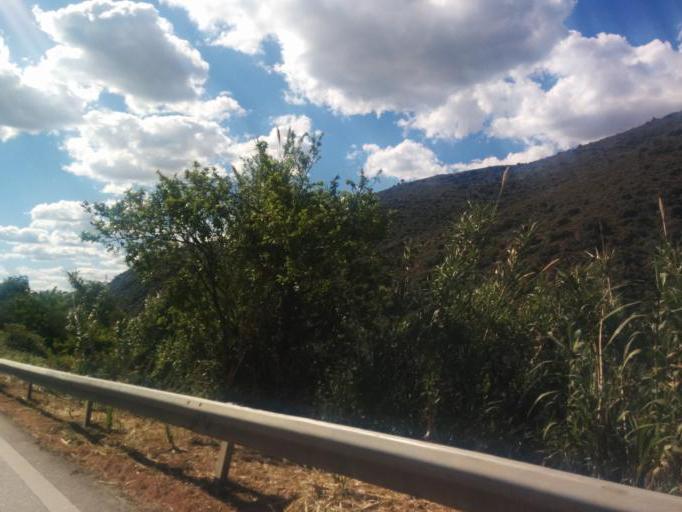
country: PT
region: Viseu
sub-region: Armamar
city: Armamar
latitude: 41.1430
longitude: -7.7108
